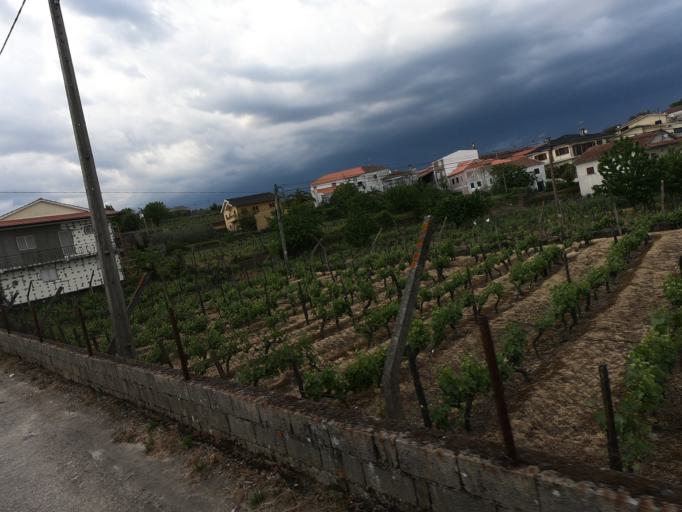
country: PT
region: Vila Real
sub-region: Sabrosa
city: Vilela
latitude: 41.2073
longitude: -7.6596
